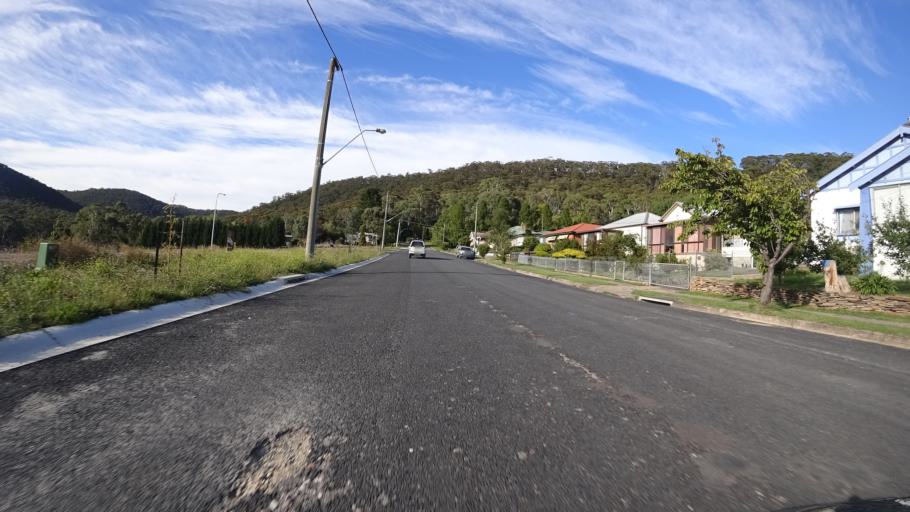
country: AU
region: New South Wales
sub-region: Lithgow
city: Lithgow
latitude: -33.4923
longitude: 150.1503
